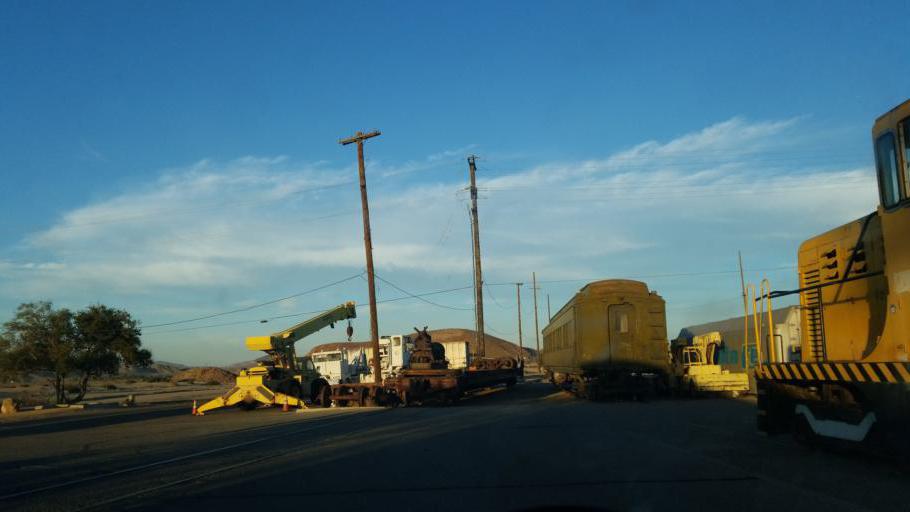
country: US
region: California
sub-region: San Bernardino County
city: Barstow
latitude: 34.9047
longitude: -117.0230
